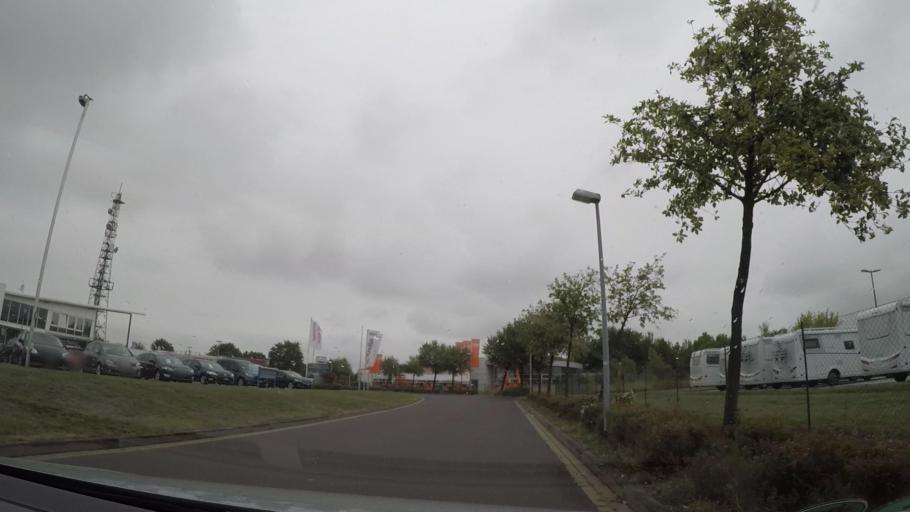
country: DE
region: Saxony-Anhalt
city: Neue Neustadt
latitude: 52.1650
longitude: 11.6048
